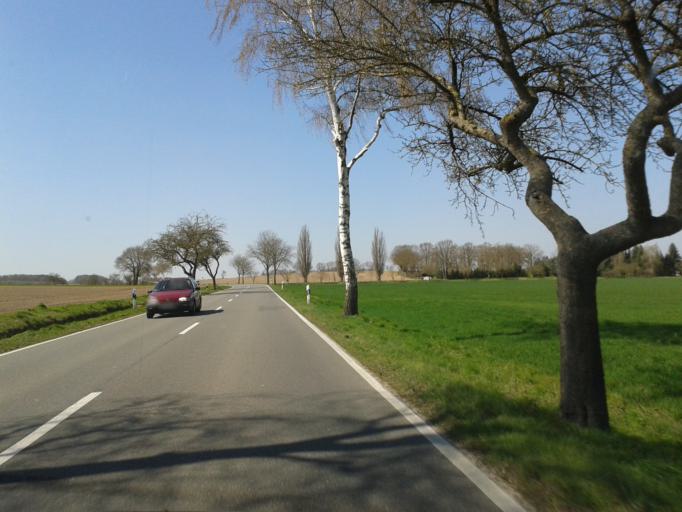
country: DE
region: Lower Saxony
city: Clenze
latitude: 52.9371
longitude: 11.0193
